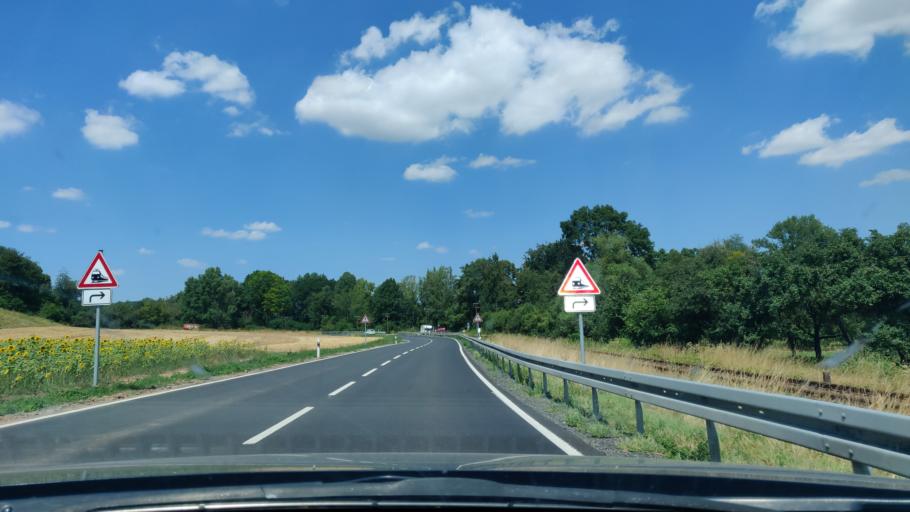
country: DE
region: Hesse
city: Fritzlar
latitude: 51.1210
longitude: 9.2490
